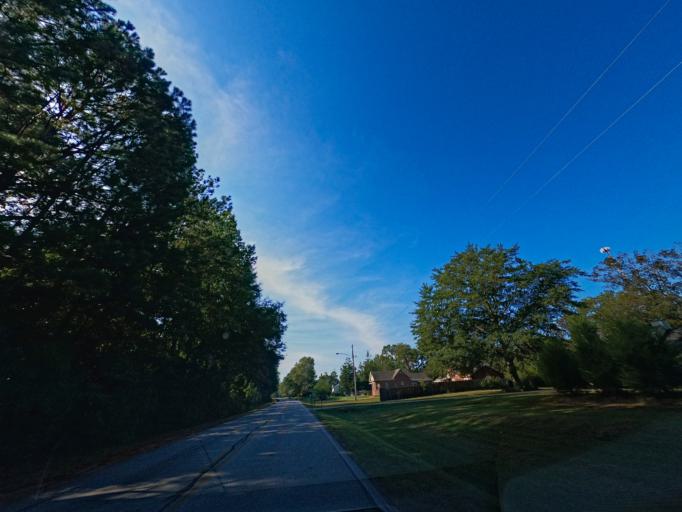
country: US
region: Georgia
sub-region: Troup County
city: Hogansville
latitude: 33.2360
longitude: -84.9432
